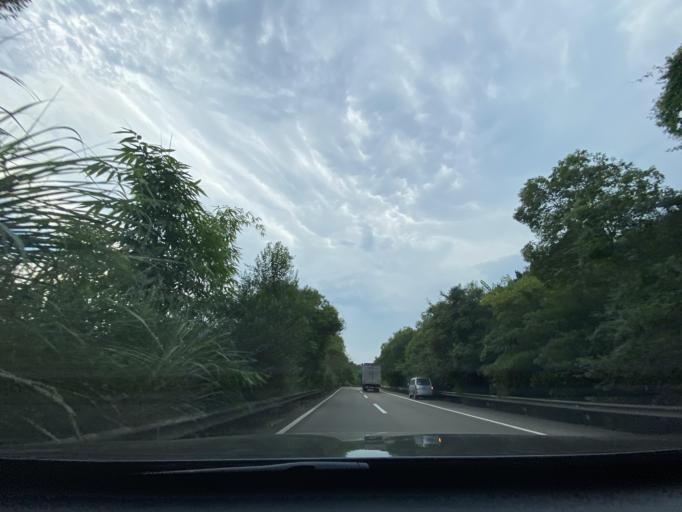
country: CN
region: Sichuan
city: Neijiang
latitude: 29.6801
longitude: 104.9577
